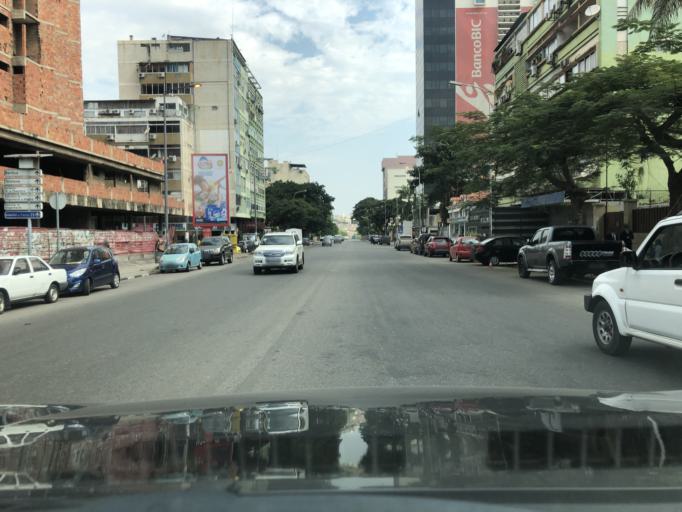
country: AO
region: Luanda
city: Luanda
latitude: -8.8235
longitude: 13.2288
